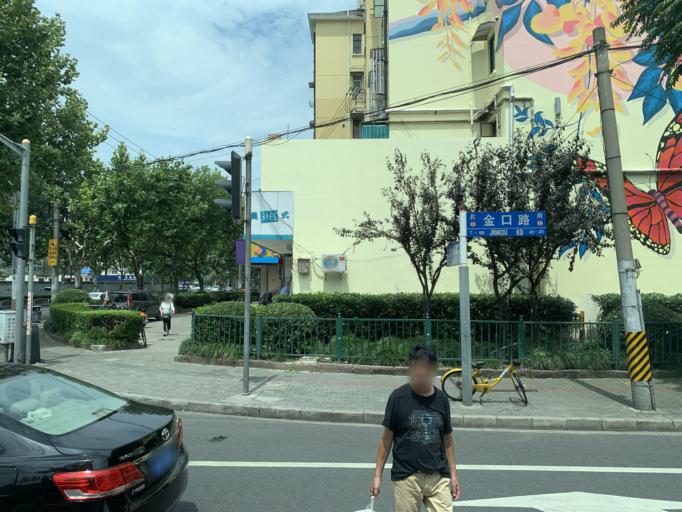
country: CN
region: Shanghai Shi
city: Pudong
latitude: 31.2499
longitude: 121.5746
